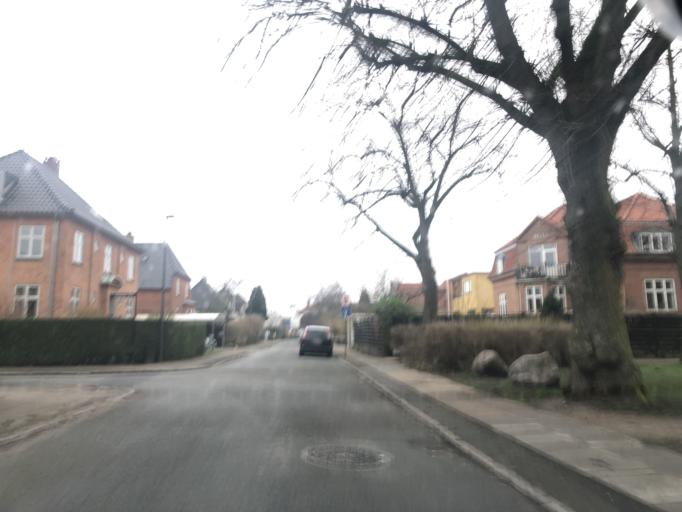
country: DK
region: Capital Region
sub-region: Tarnby Kommune
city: Tarnby
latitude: 55.6524
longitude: 12.6073
